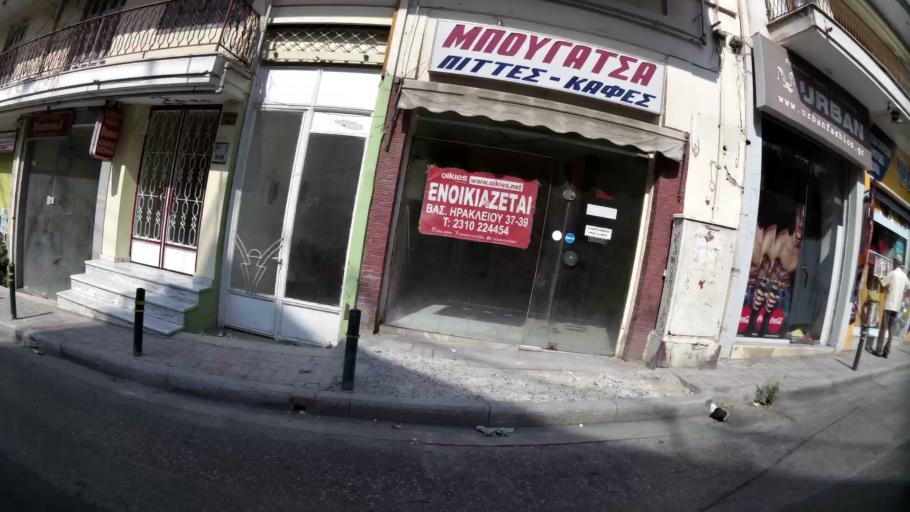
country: GR
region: Central Macedonia
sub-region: Nomos Thessalonikis
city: Sykies
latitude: 40.6475
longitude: 22.9509
